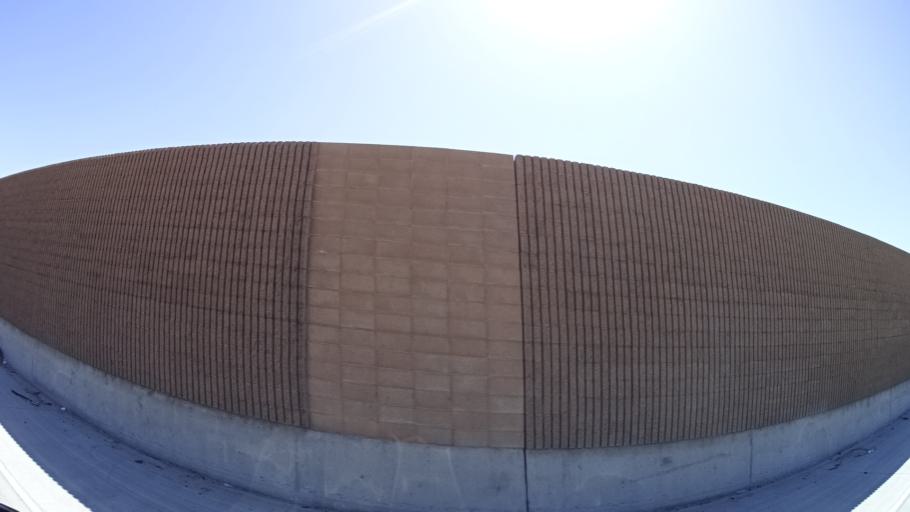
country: US
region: California
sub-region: Los Angeles County
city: San Fernando
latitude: 34.2367
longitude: -118.4144
